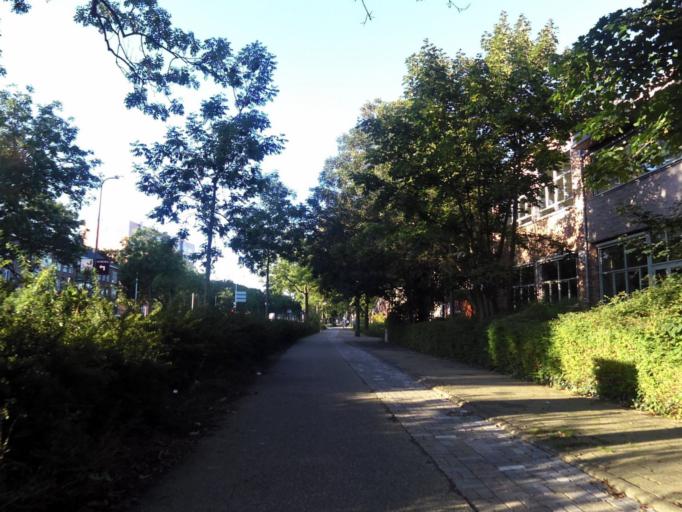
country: NL
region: South Holland
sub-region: Gemeente Alphen aan den Rijn
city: Alphen aan den Rijn
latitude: 52.1333
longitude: 4.6569
